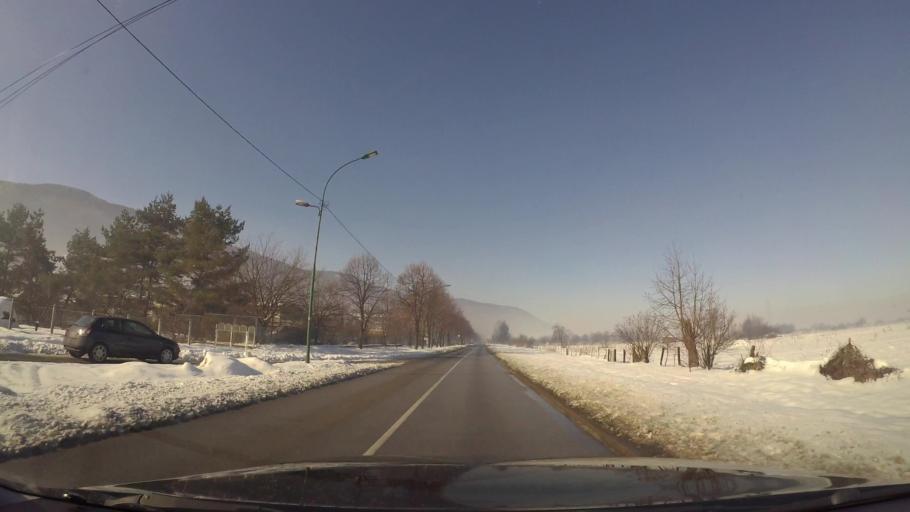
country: BA
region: Federation of Bosnia and Herzegovina
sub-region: Kanton Sarajevo
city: Sarajevo
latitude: 43.7943
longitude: 18.3250
